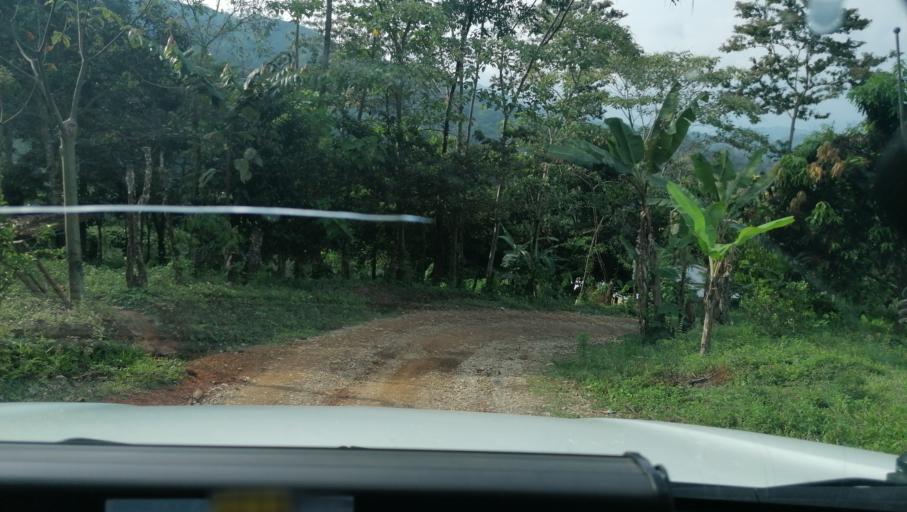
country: MX
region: Chiapas
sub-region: Tapilula
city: San Francisco Jacona
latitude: 17.3255
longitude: -93.0994
